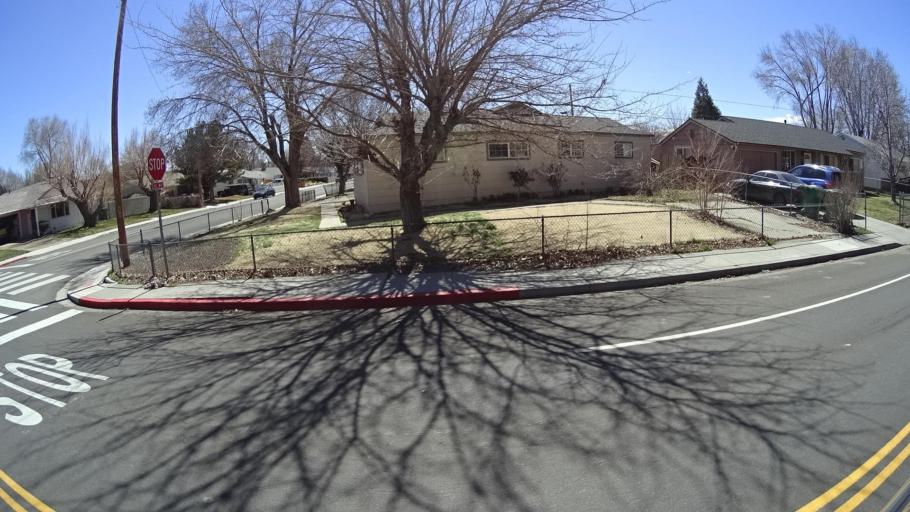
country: US
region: Nevada
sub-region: Washoe County
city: Sparks
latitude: 39.5529
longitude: -119.7579
